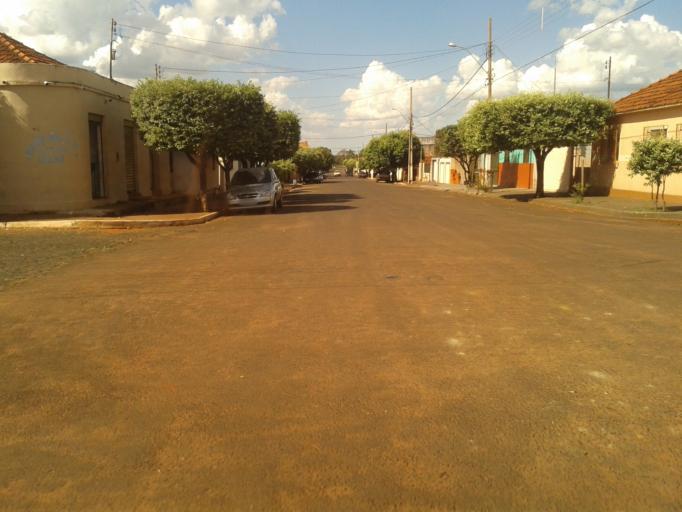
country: BR
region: Minas Gerais
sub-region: Santa Vitoria
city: Santa Vitoria
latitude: -18.6938
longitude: -49.9433
